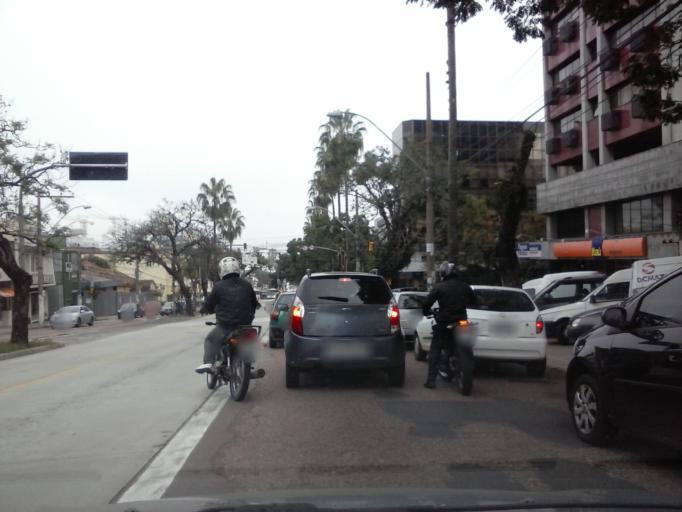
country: BR
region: Rio Grande do Sul
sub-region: Porto Alegre
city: Porto Alegre
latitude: -30.0392
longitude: -51.1762
